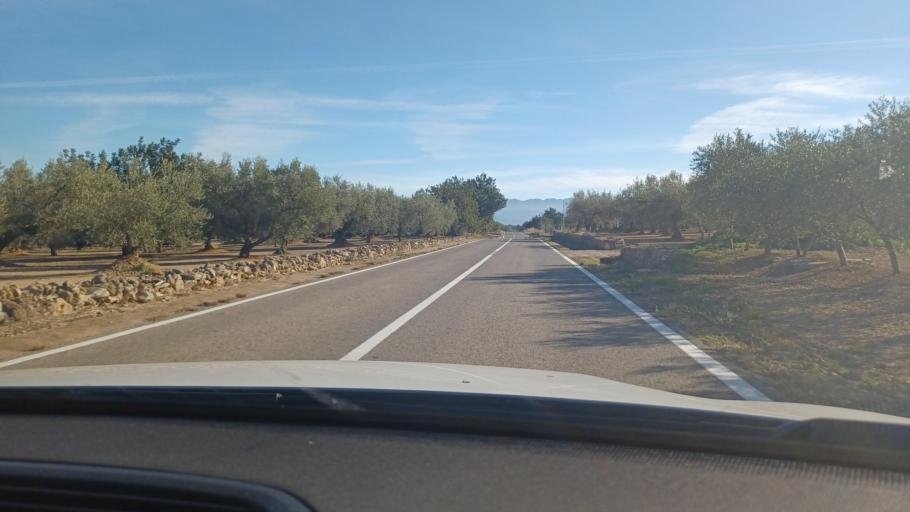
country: ES
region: Catalonia
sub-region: Provincia de Tarragona
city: Mas de Barberans
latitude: 40.7197
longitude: 0.3980
